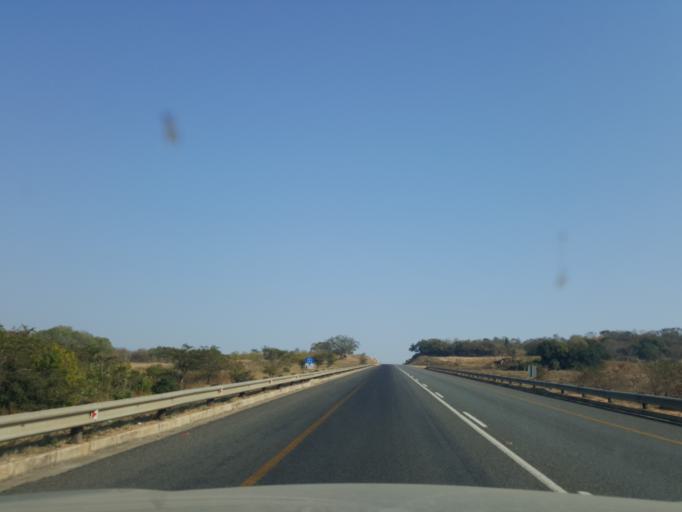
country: ZA
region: Mpumalanga
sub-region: Ehlanzeni District
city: Nelspruit
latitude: -25.4503
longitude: 31.0136
